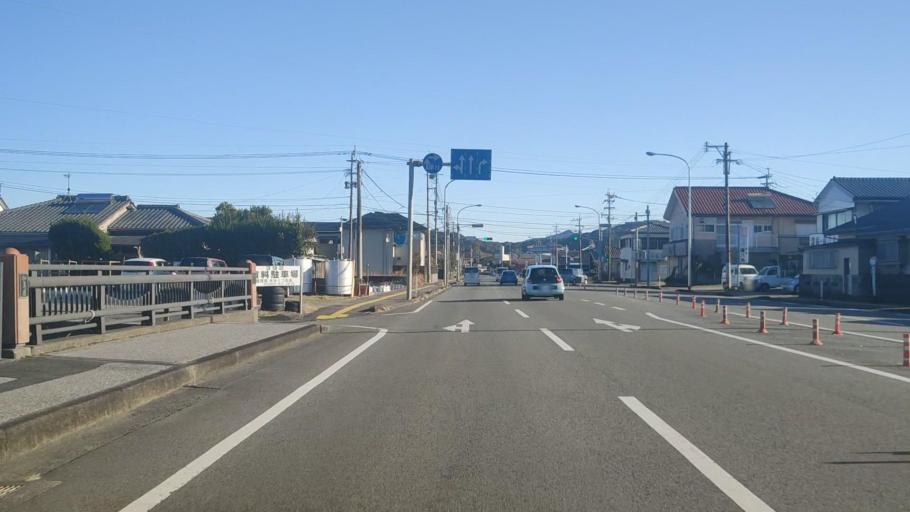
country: JP
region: Miyazaki
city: Nobeoka
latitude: 32.4842
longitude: 131.6605
